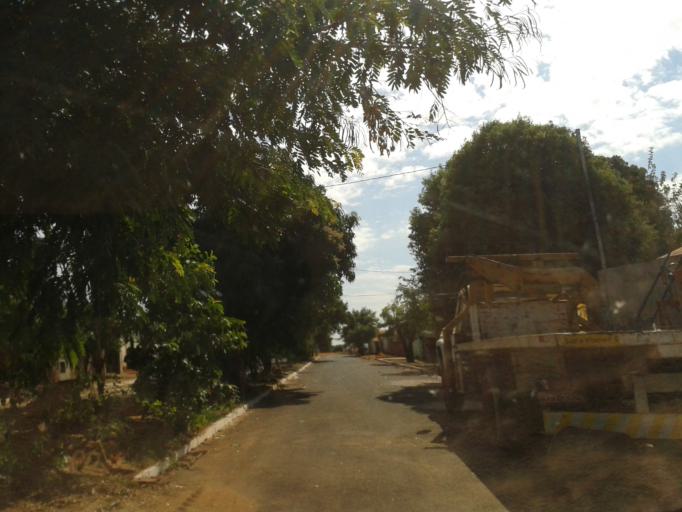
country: BR
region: Minas Gerais
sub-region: Santa Vitoria
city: Santa Vitoria
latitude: -18.8407
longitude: -50.1165
